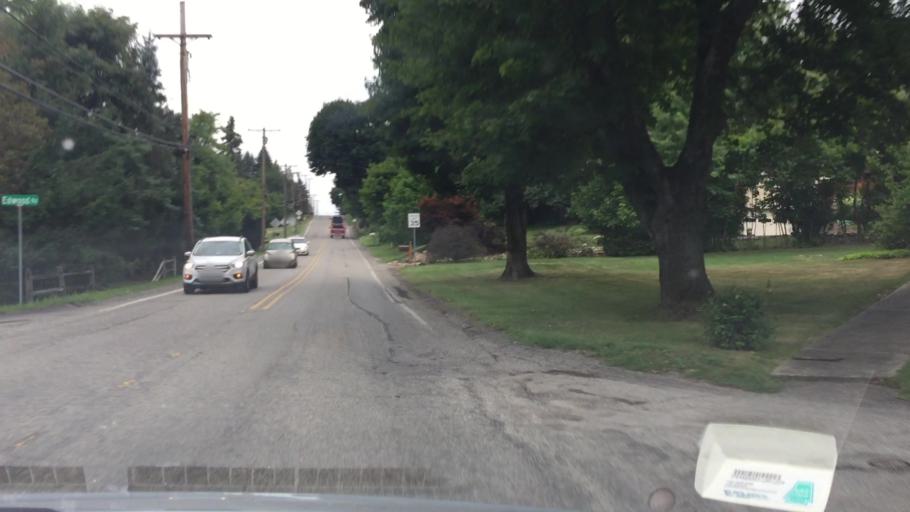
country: US
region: Pennsylvania
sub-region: Allegheny County
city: West View
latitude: 40.5588
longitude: -80.0325
